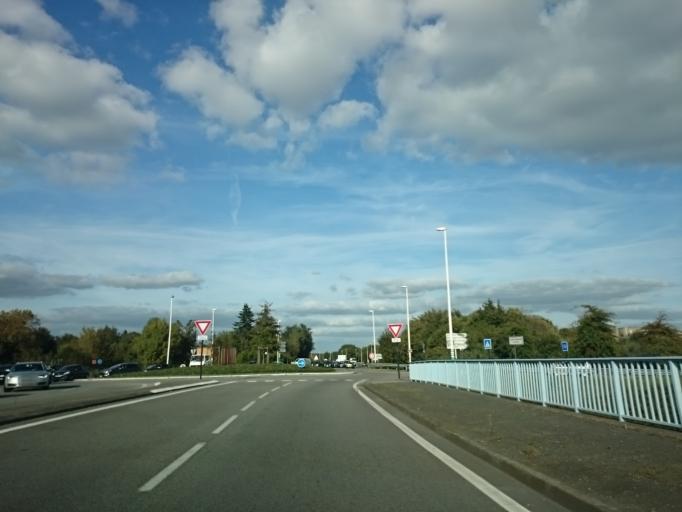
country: FR
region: Pays de la Loire
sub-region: Departement de la Loire-Atlantique
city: Saint-Herblain
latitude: 47.2339
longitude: -1.6464
